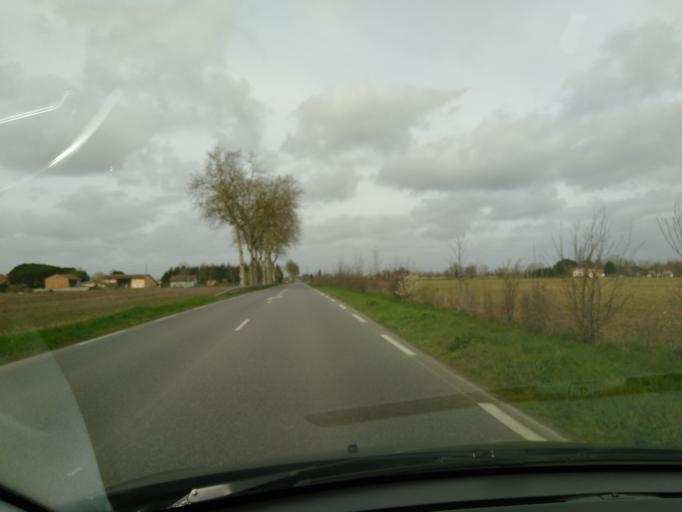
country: FR
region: Midi-Pyrenees
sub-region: Departement de la Haute-Garonne
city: Merville
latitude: 43.7369
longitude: 1.3148
